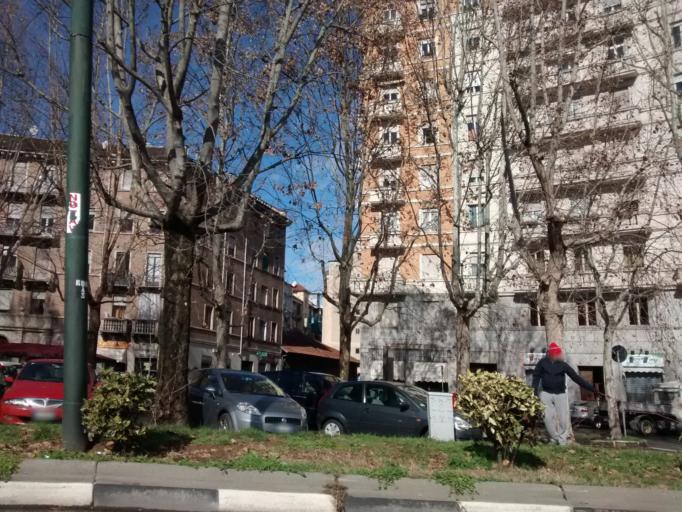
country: IT
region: Piedmont
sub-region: Provincia di Torino
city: Lesna
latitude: 45.0758
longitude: 7.6432
